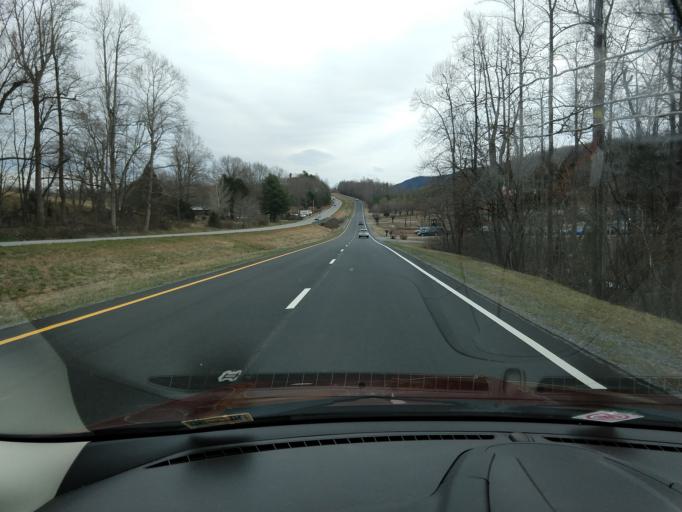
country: US
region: Virginia
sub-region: Franklin County
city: Henry Fork
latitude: 36.8488
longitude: -79.8869
